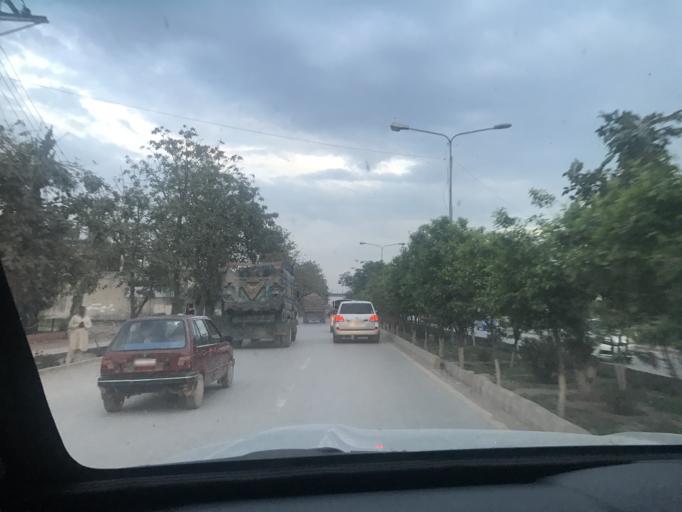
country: PK
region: Khyber Pakhtunkhwa
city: Peshawar
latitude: 33.9769
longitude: 71.4493
